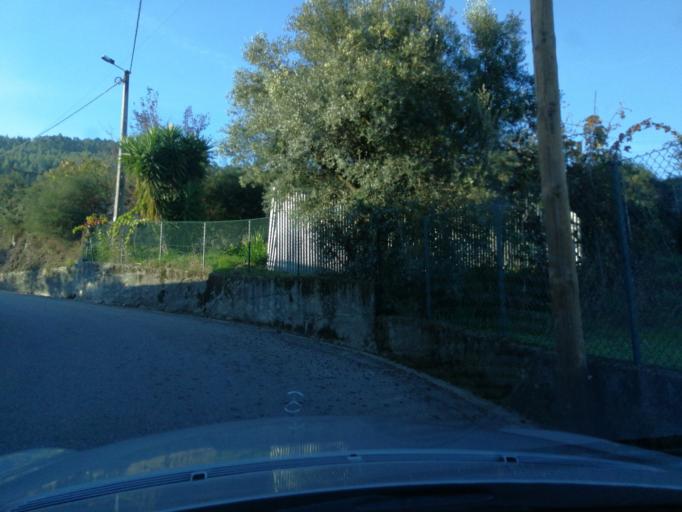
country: PT
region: Braga
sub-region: Braga
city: Oliveira
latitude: 41.4607
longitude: -8.4500
